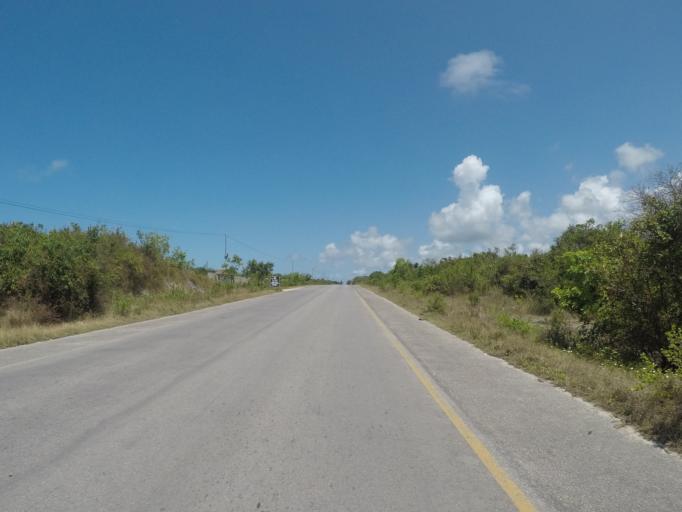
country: TZ
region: Zanzibar Central/South
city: Nganane
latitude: -6.2925
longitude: 39.5372
